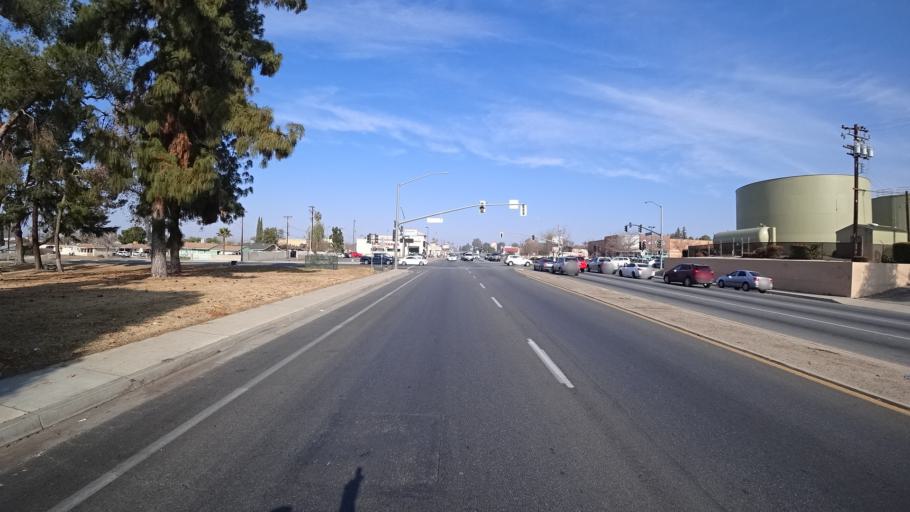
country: US
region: California
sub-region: Kern County
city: Bakersfield
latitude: 35.3897
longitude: -118.9676
